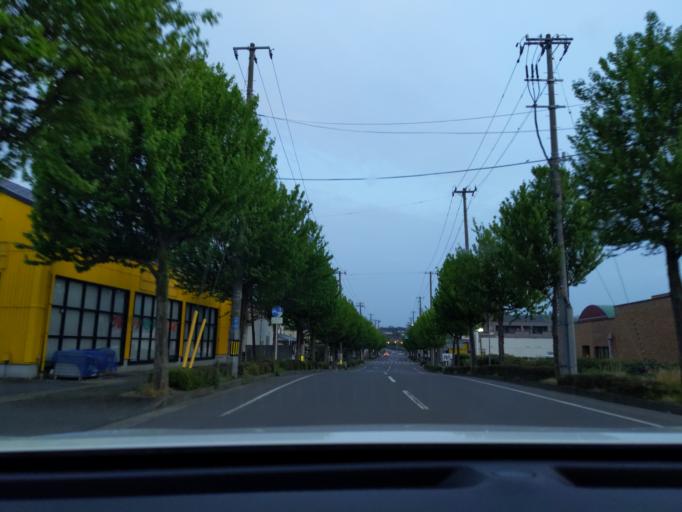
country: JP
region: Fukushima
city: Sukagawa
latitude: 37.2941
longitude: 140.3635
